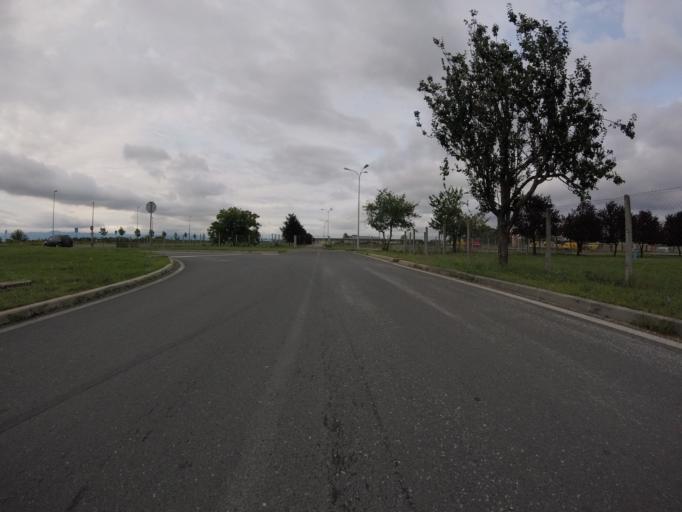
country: HR
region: Zagrebacka
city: Gradici
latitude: 45.7129
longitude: 16.0449
